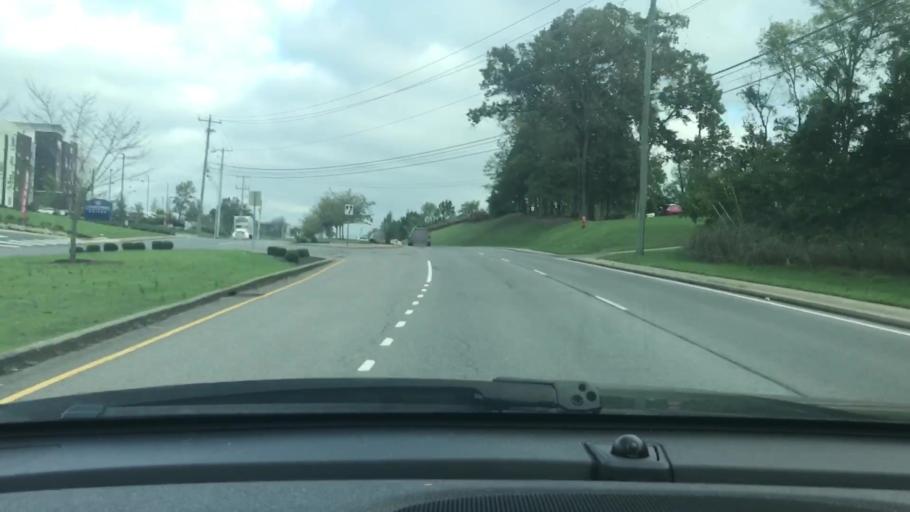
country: US
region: Tennessee
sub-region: Davidson County
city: Goodlettsville
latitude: 36.3157
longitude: -86.6991
